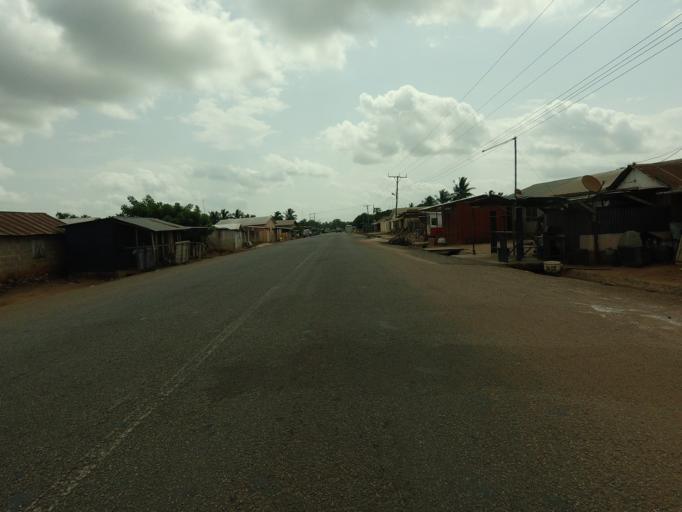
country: TG
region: Maritime
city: Lome
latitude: 6.2227
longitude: 1.0330
